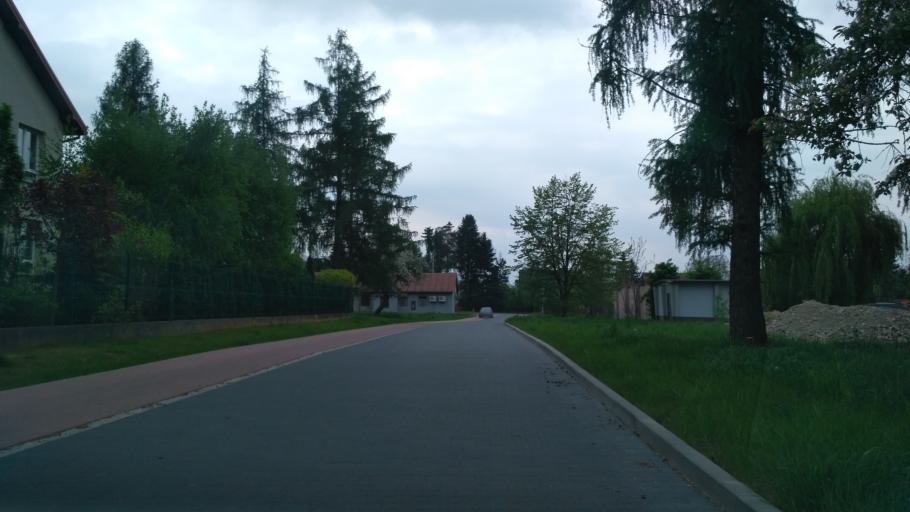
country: PL
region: Lesser Poland Voivodeship
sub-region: Powiat tarnowski
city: Tarnowiec
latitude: 49.9838
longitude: 20.9843
